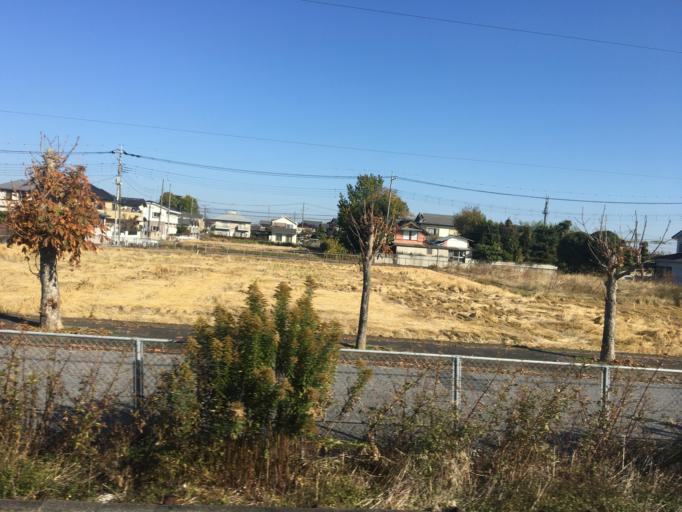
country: JP
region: Saitama
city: Kazo
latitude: 36.1171
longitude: 139.6126
